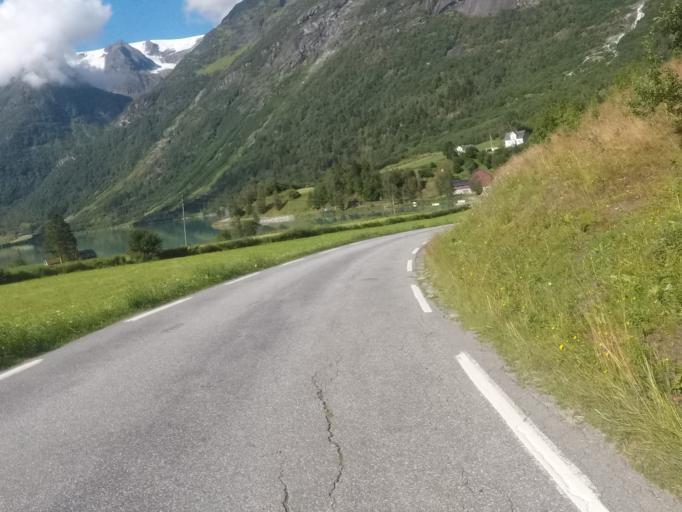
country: NO
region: Sogn og Fjordane
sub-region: Stryn
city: Stryn
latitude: 61.7573
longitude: 6.8160
